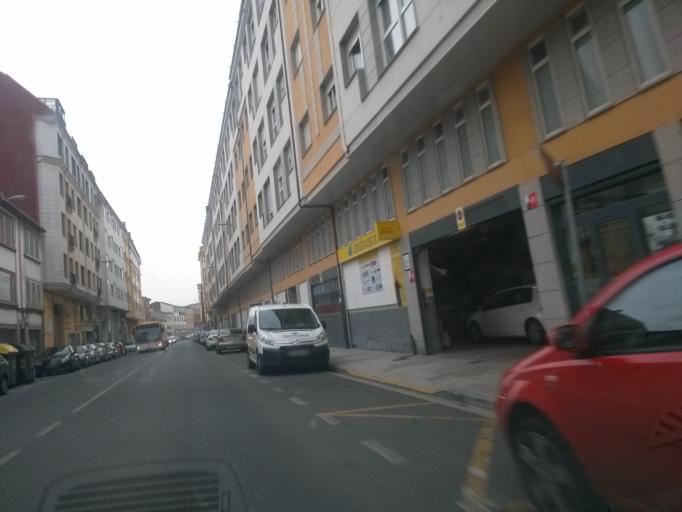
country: ES
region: Galicia
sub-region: Provincia de Lugo
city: Lugo
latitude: 43.0189
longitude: -7.5478
